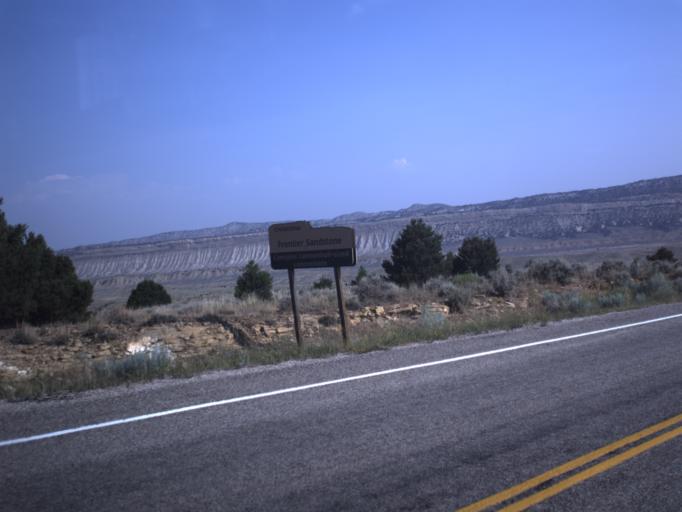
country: US
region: Utah
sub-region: Daggett County
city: Manila
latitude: 40.9631
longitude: -109.4691
